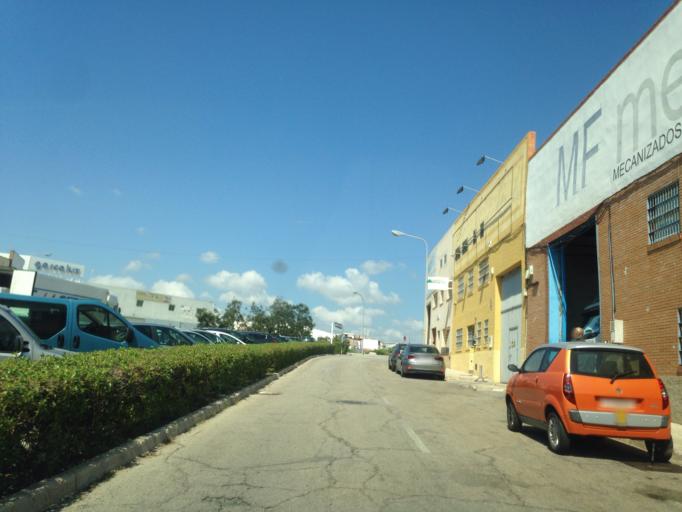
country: ES
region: Andalusia
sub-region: Provincia de Malaga
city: Malaga
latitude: 36.7060
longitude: -4.4777
